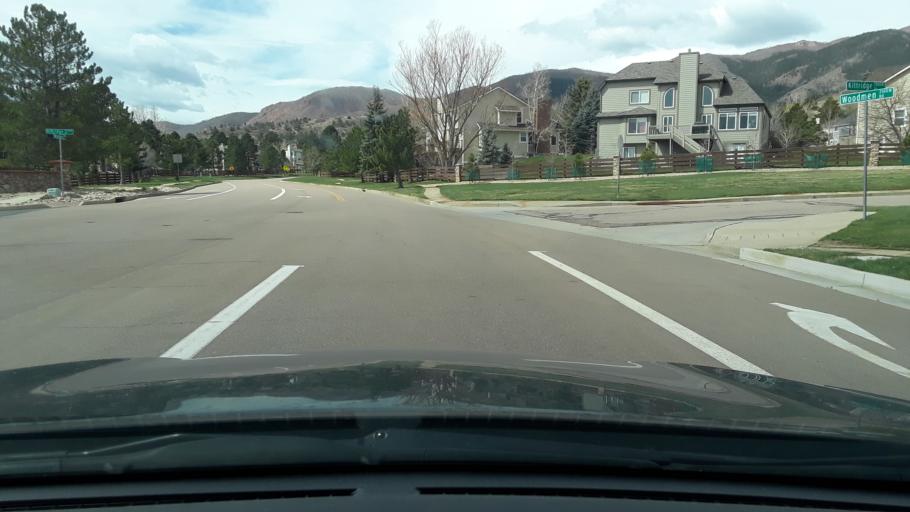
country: US
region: Colorado
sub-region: El Paso County
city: Air Force Academy
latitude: 38.9507
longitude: -104.8651
